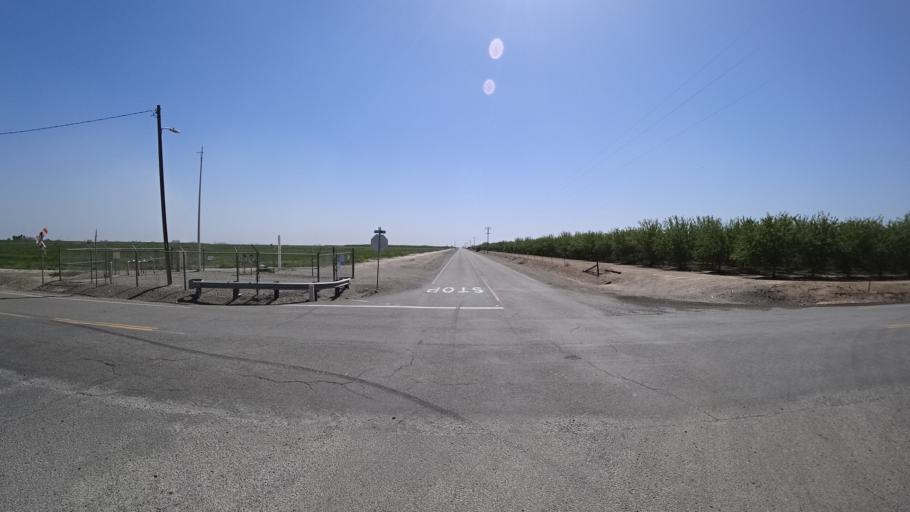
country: US
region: California
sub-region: Glenn County
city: Willows
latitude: 39.5822
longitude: -122.1371
